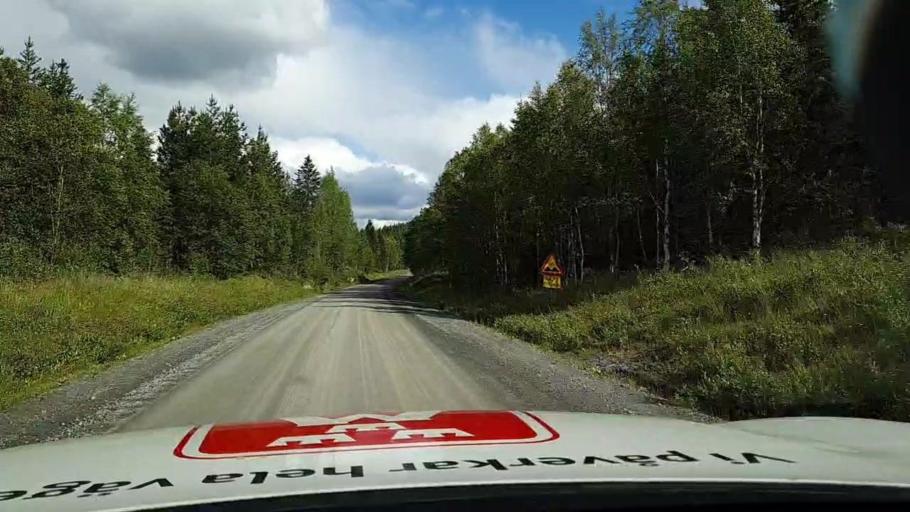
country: SE
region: Jaemtland
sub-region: Krokoms Kommun
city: Valla
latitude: 63.6774
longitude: 13.6834
